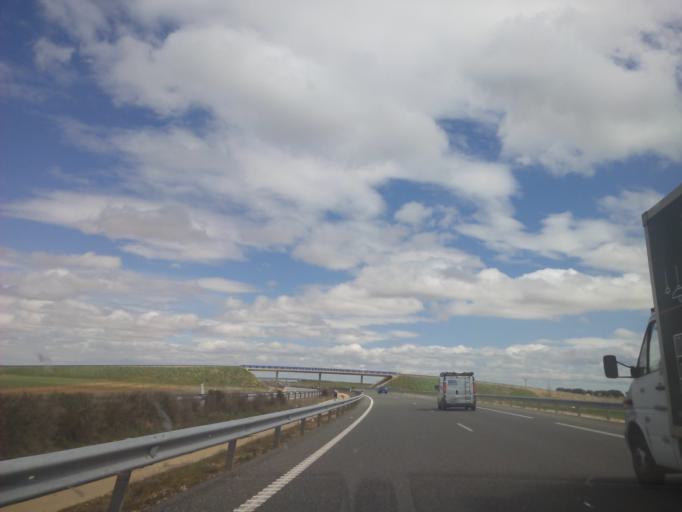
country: ES
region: Castille and Leon
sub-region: Provincia de Salamanca
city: Pelabravo
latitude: 40.9289
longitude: -5.5783
